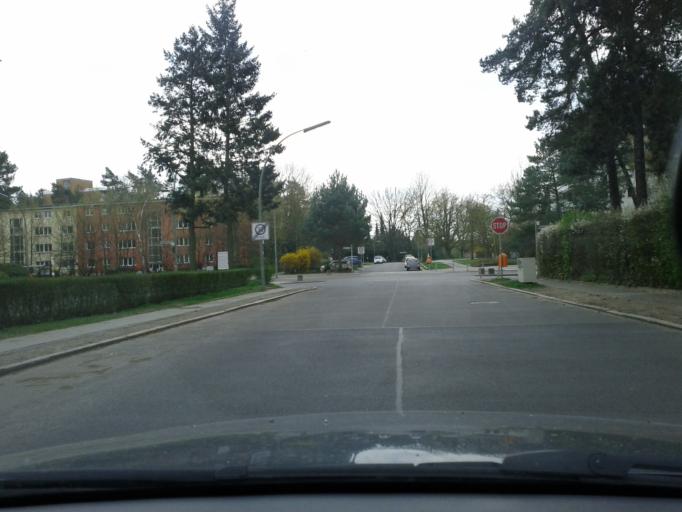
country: DE
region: Berlin
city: Zehlendorf Bezirk
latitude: 52.4520
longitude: 13.2627
